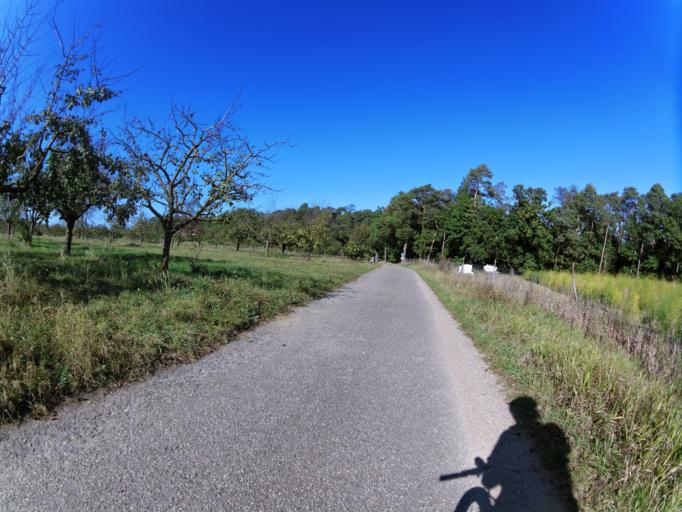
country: DE
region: Bavaria
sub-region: Regierungsbezirk Unterfranken
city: Sommerhausen
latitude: 49.6907
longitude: 10.0448
